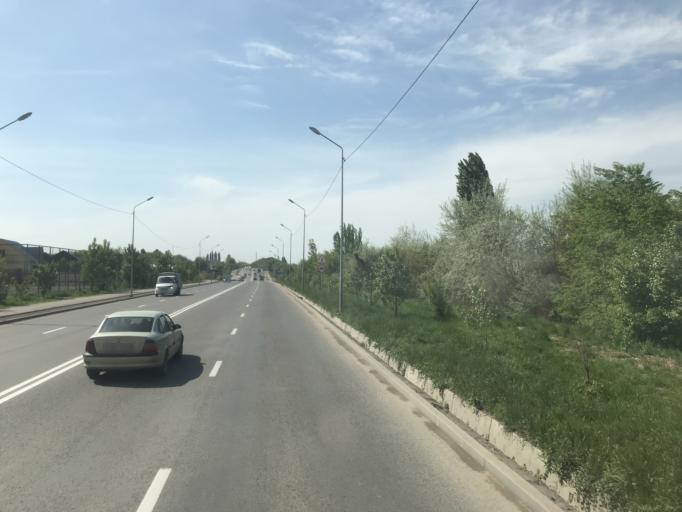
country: KZ
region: Almaty Oblysy
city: Burunday
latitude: 43.3093
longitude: 76.8721
